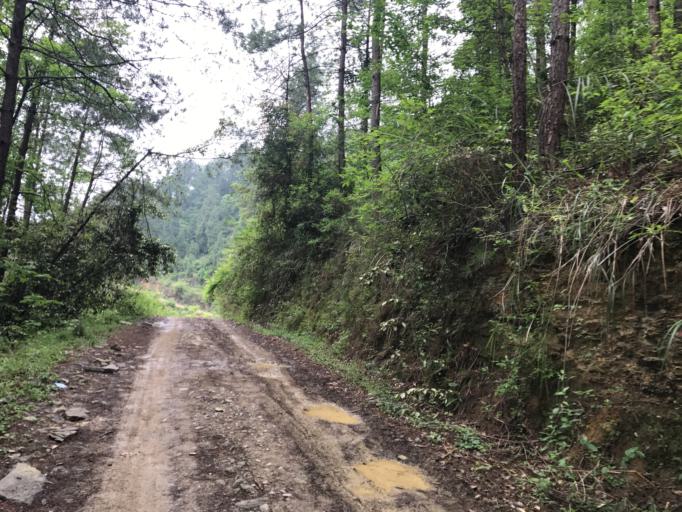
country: CN
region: Guizhou Sheng
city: Xujiaba
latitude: 27.7268
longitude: 108.0140
